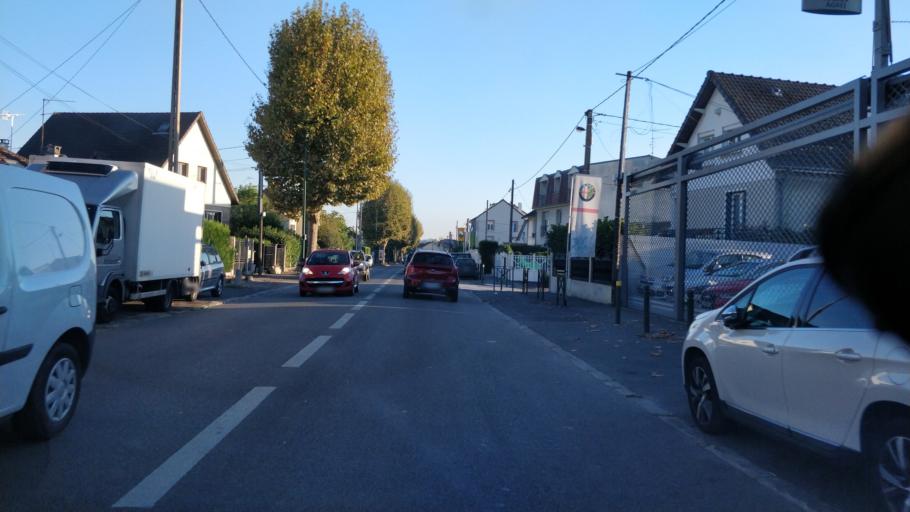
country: FR
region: Ile-de-France
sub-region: Departement de Seine-Saint-Denis
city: Neuilly-sur-Marne
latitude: 48.8720
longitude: 2.5539
